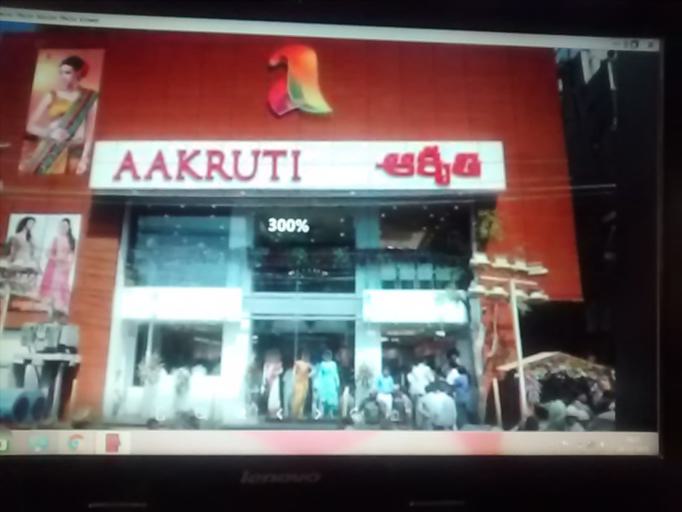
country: IN
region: Andhra Pradesh
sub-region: Prakasam
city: Chirala
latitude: 15.8258
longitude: 80.3574
